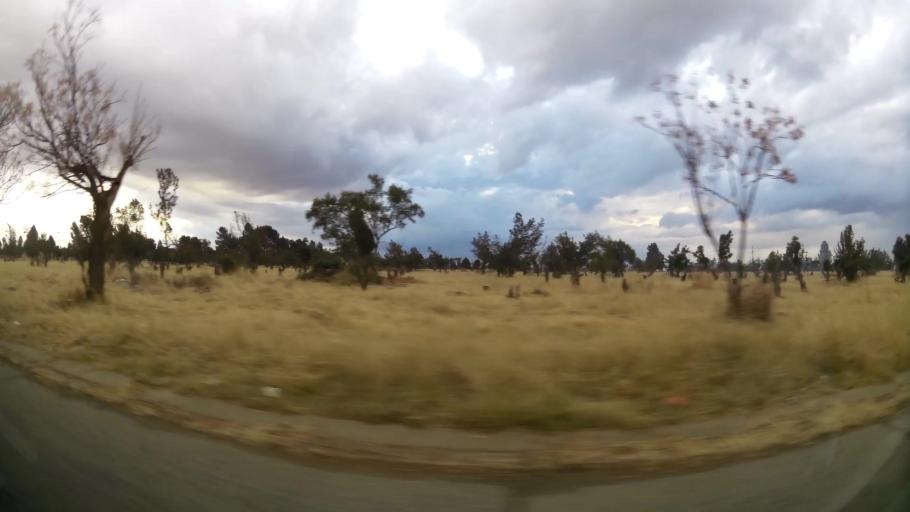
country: ZA
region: Orange Free State
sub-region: Lejweleputswa District Municipality
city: Welkom
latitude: -27.9612
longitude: 26.7193
